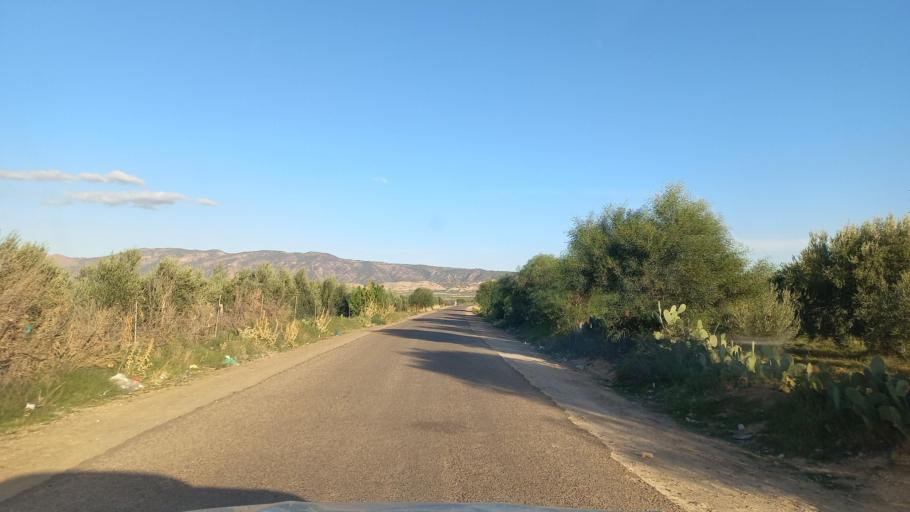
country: TN
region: Al Qasrayn
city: Sbiba
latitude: 35.4132
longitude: 9.1252
